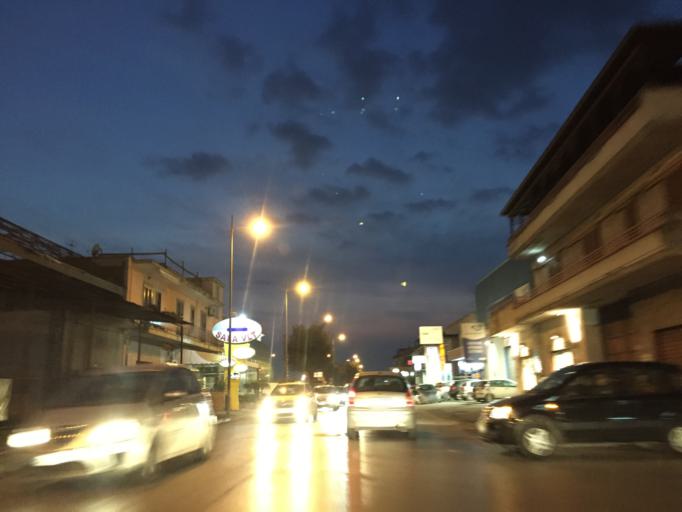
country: IT
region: Campania
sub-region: Provincia di Salerno
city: San Lorenzo
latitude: 40.7481
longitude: 14.5872
